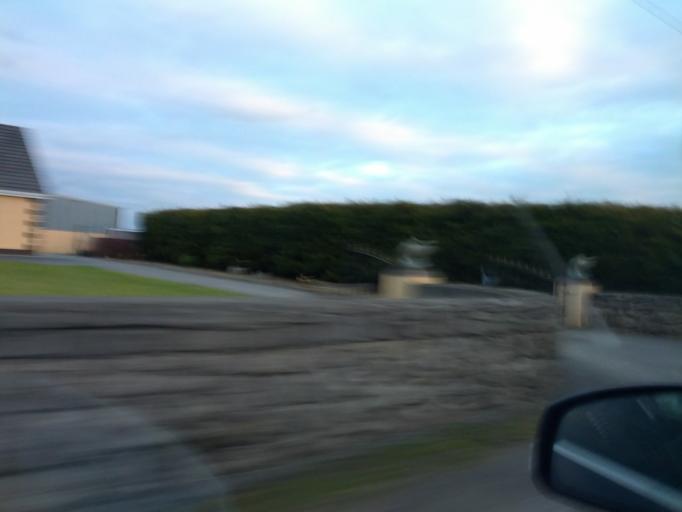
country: IE
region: Connaught
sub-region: County Galway
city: Athenry
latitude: 53.3264
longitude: -8.7651
